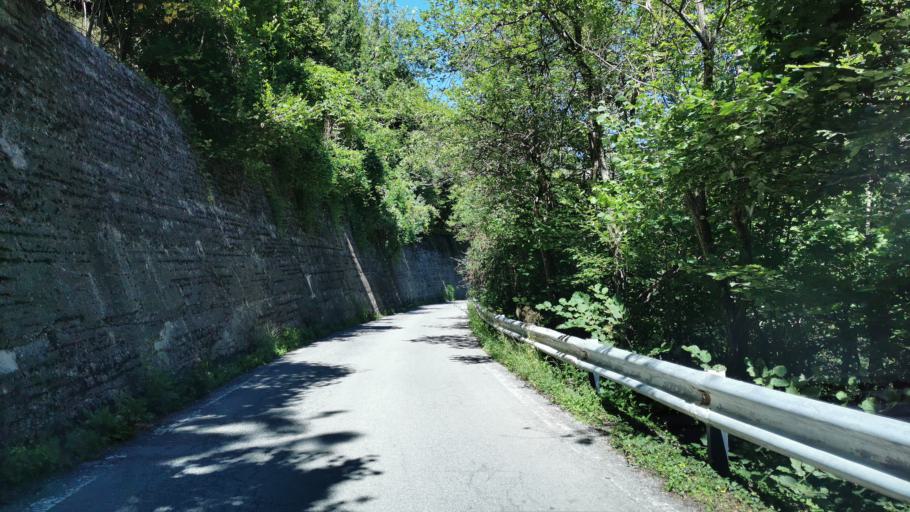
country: IT
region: Piedmont
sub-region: Provincia di Cuneo
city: Entracque
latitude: 44.2155
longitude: 7.3842
